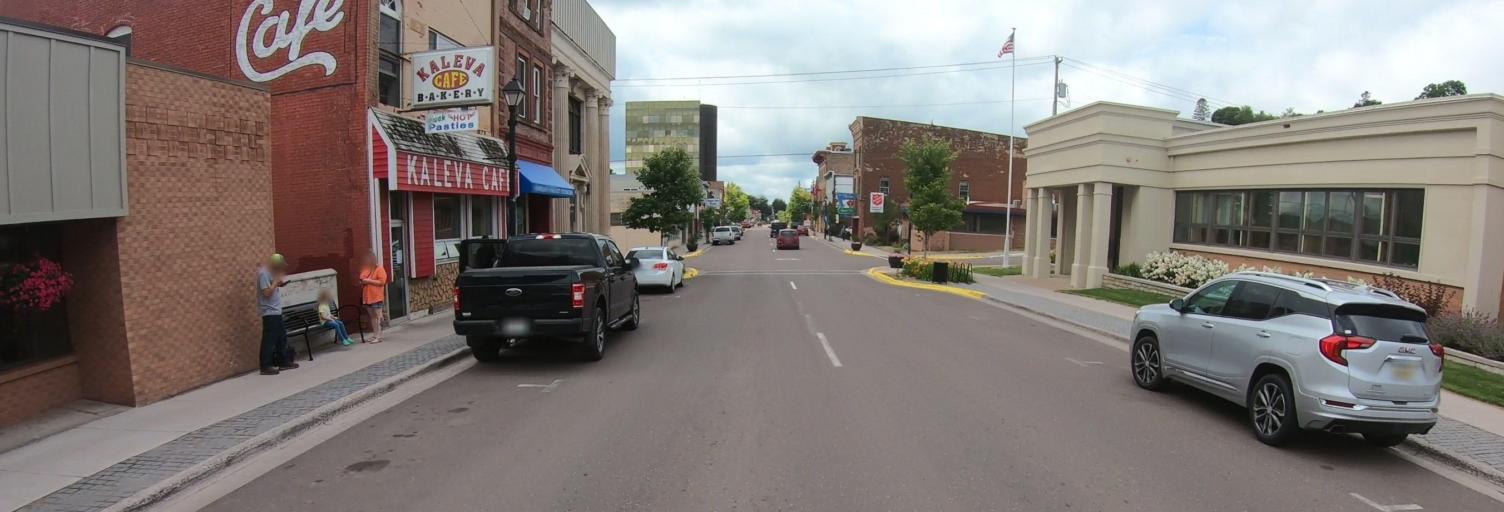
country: US
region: Michigan
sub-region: Houghton County
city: Hancock
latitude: 47.1268
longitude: -88.5824
